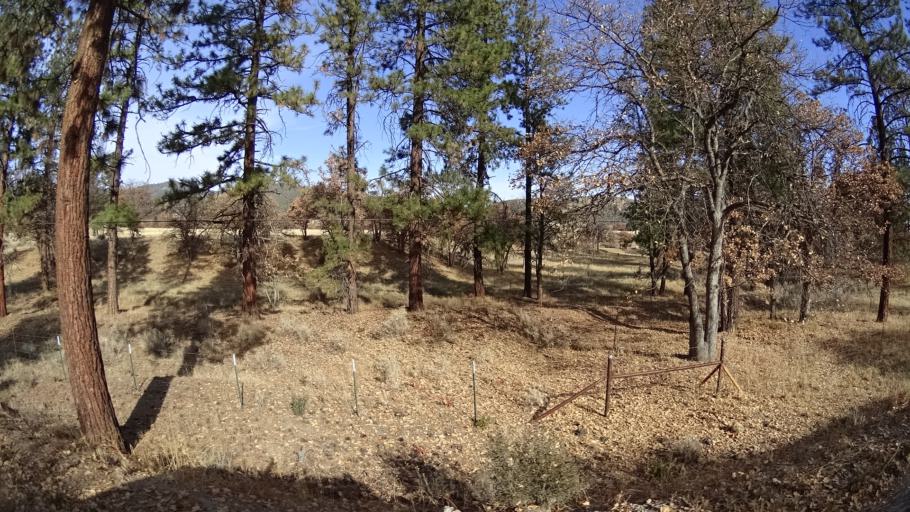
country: US
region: California
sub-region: Siskiyou County
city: Montague
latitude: 41.5412
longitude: -122.5912
